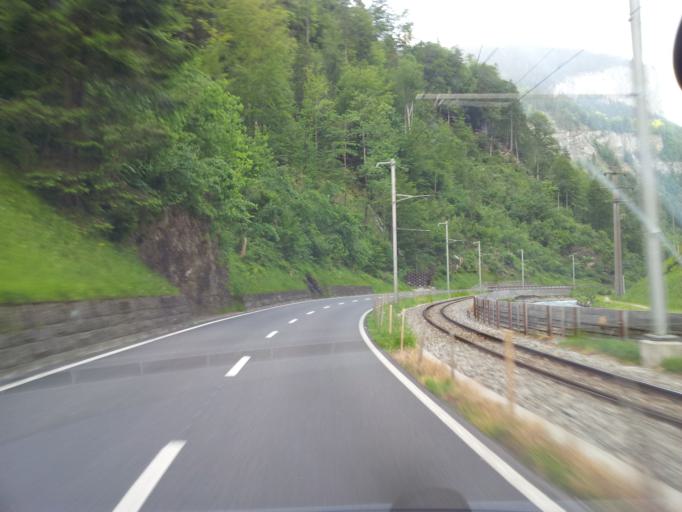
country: CH
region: Bern
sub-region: Interlaken-Oberhasli District
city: Lauterbrunnen
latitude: 46.6079
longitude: 7.9039
